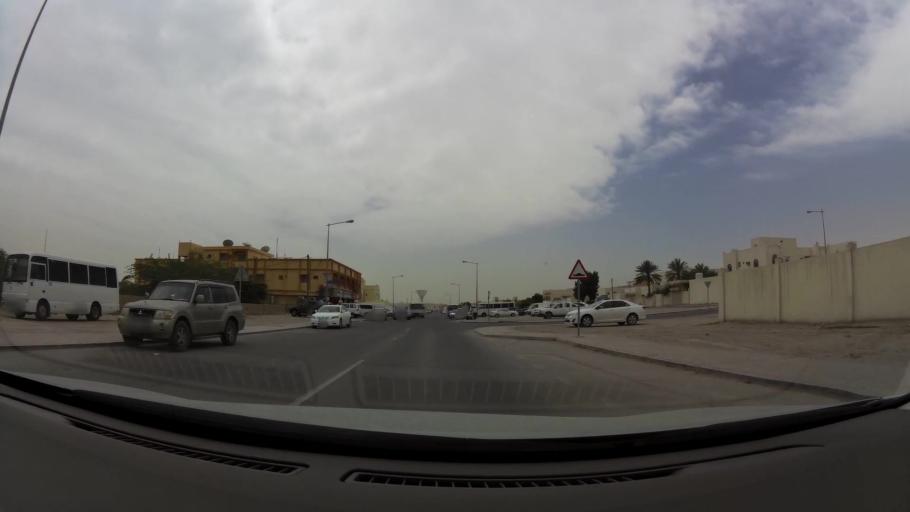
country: QA
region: Baladiyat ar Rayyan
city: Ar Rayyan
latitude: 25.2905
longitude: 51.4590
